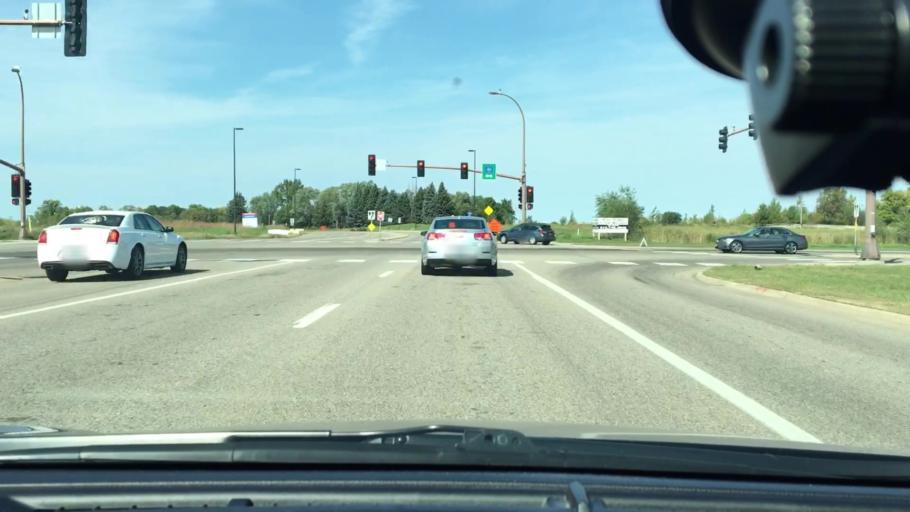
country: US
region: Minnesota
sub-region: Hennepin County
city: Corcoran
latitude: 45.0856
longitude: -93.5167
